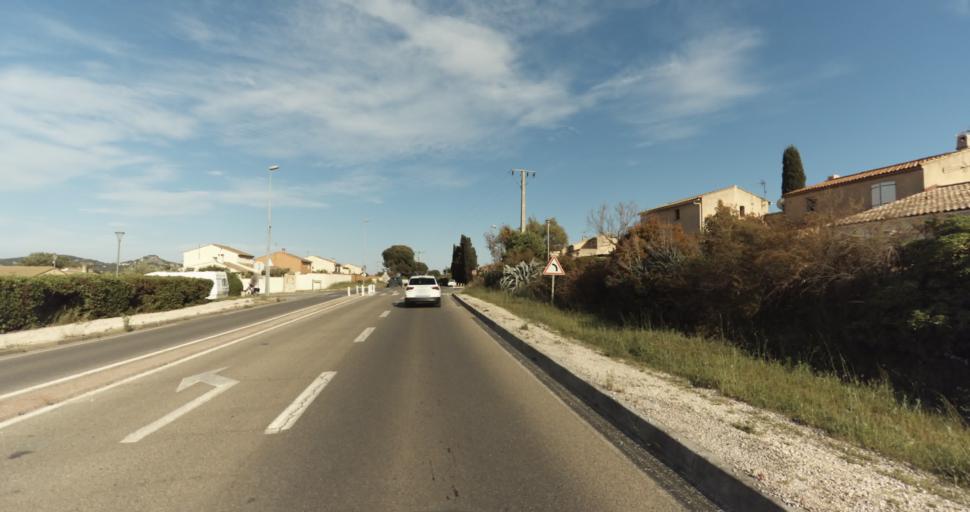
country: FR
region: Provence-Alpes-Cote d'Azur
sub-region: Departement du Var
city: Carqueiranne
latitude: 43.1180
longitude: 6.0790
